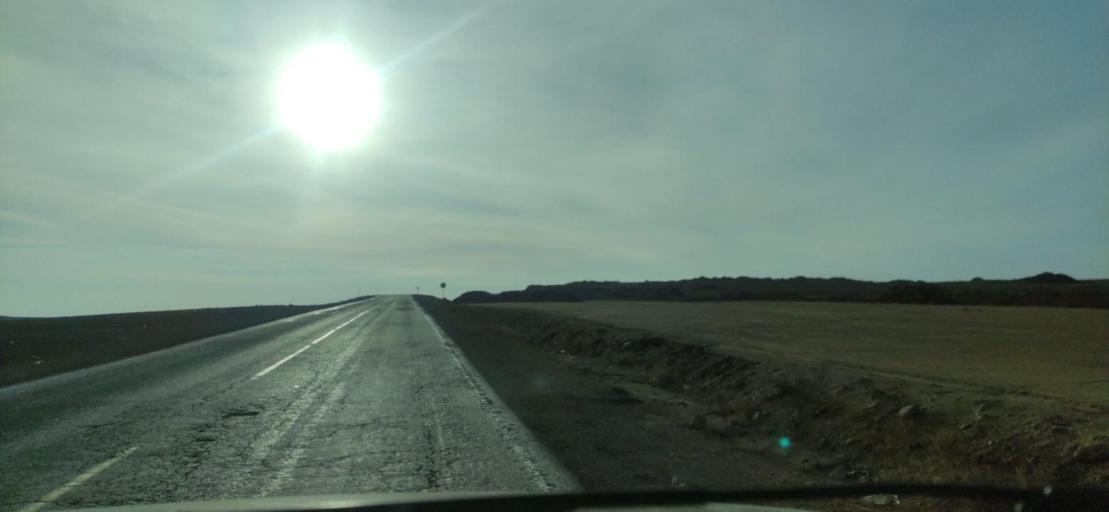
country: KZ
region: Qaraghandy
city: Saryshaghan
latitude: 46.3265
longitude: 73.7928
